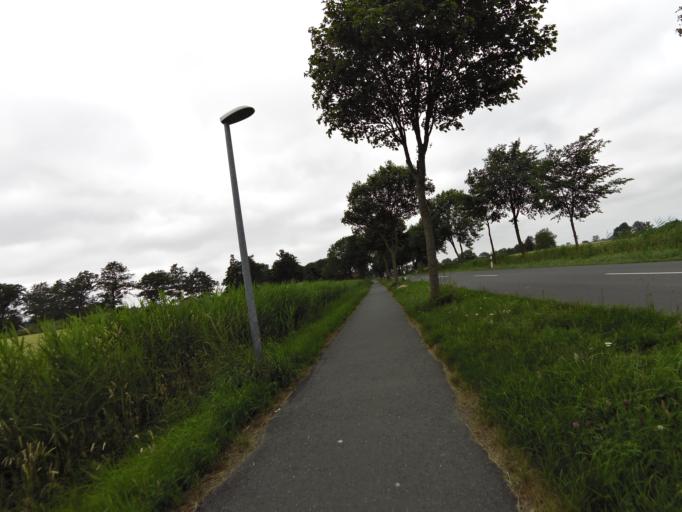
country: DE
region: Lower Saxony
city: Padingbuttel
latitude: 53.7125
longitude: 8.5503
